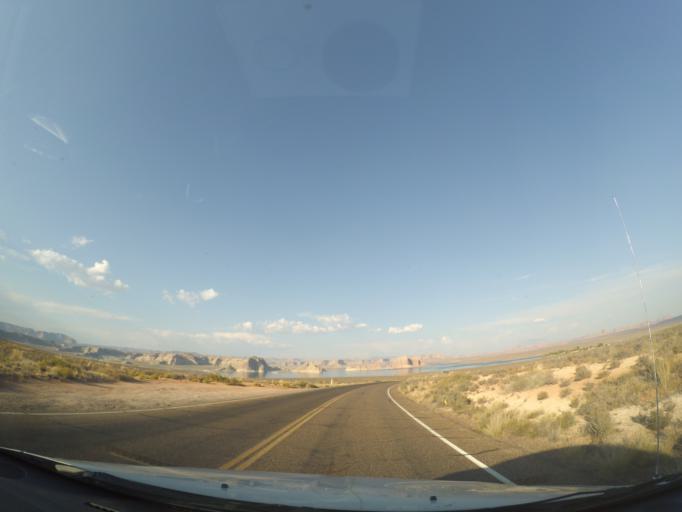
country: US
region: Arizona
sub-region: Coconino County
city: Page
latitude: 36.9918
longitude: -111.5100
